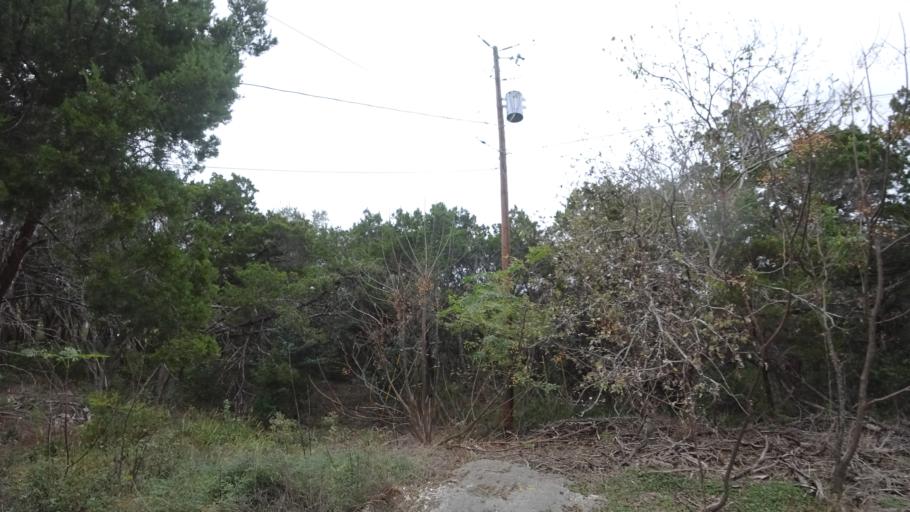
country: US
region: Texas
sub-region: Travis County
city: Barton Creek
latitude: 30.2631
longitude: -97.9150
